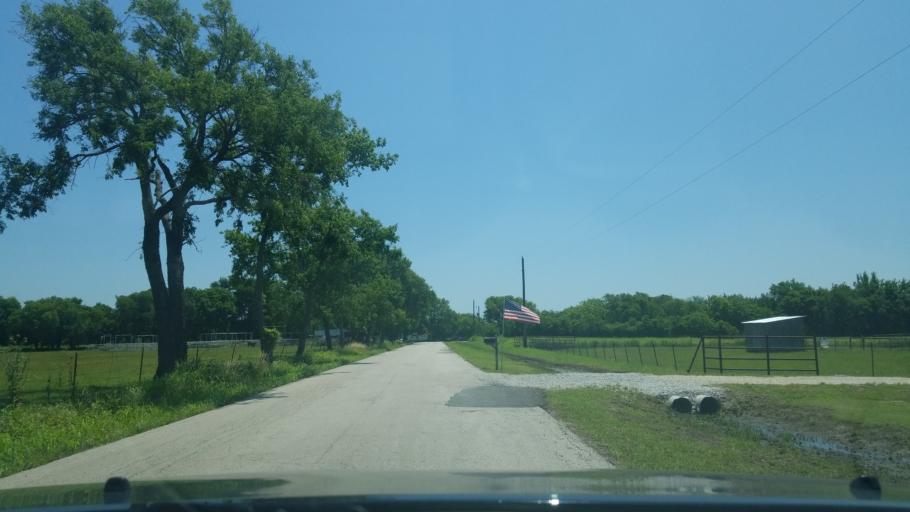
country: US
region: Texas
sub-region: Denton County
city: Sanger
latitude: 33.3418
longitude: -97.2229
